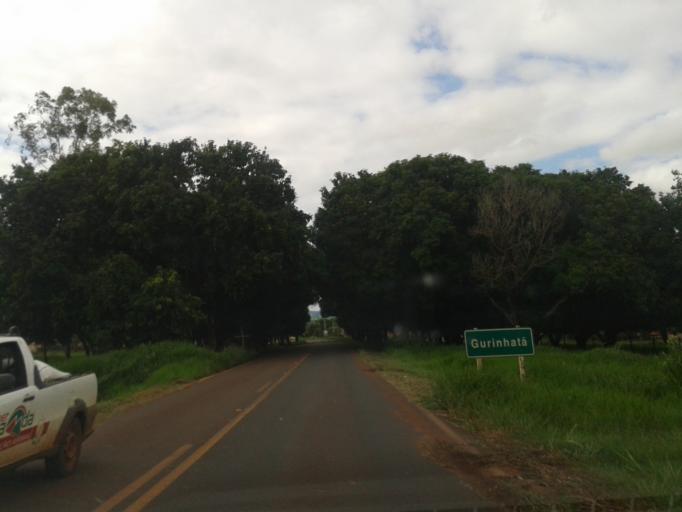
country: BR
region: Minas Gerais
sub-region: Ituiutaba
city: Ituiutaba
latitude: -19.2018
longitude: -49.7845
